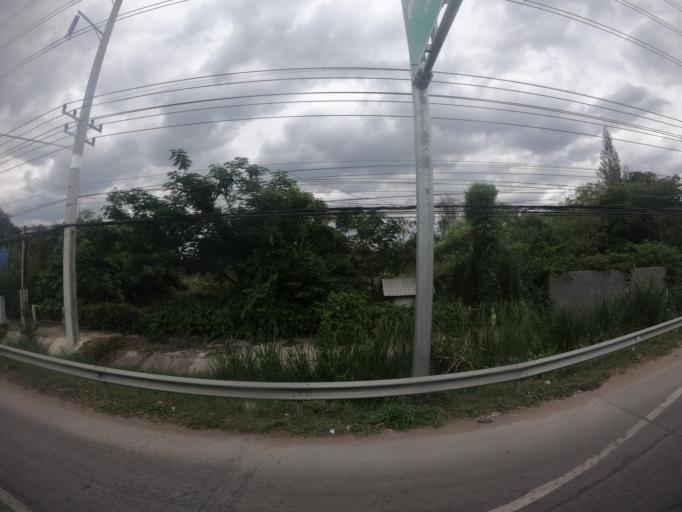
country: TH
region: Nakhon Ratchasima
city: Nakhon Ratchasima
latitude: 14.9347
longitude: 102.1356
